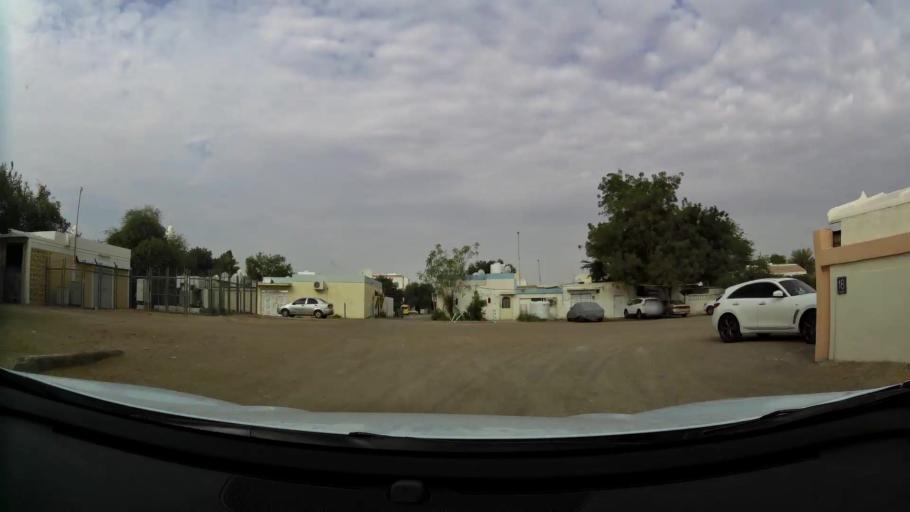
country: AE
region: Abu Dhabi
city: Al Ain
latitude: 24.2227
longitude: 55.7408
